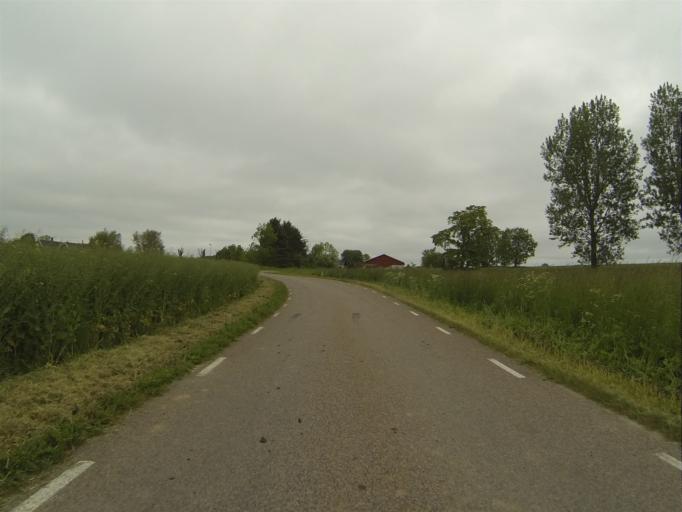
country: SE
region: Skane
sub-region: Lunds Kommun
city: Genarp
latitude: 55.6794
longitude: 13.3231
